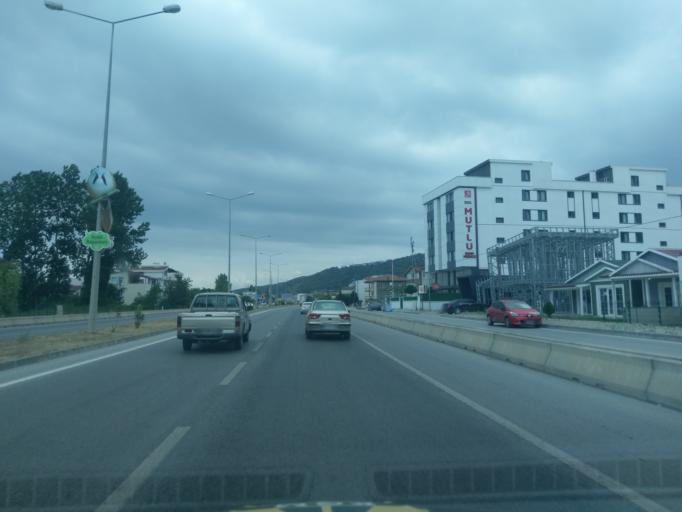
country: TR
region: Samsun
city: Taflan
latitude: 41.3935
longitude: 36.1999
